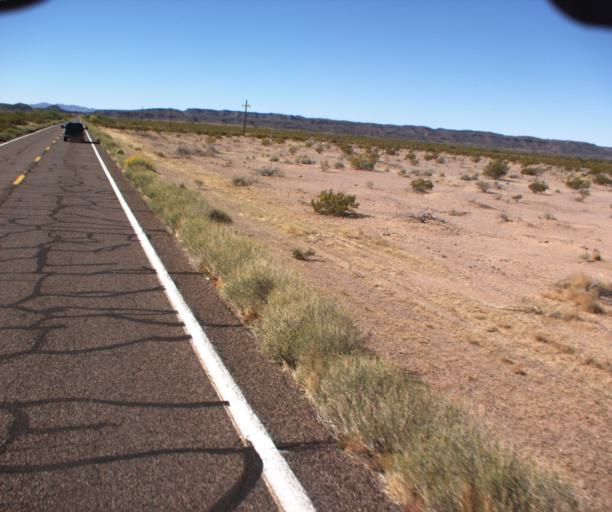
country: US
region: Arizona
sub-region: Pima County
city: Ajo
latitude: 32.6041
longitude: -112.8697
